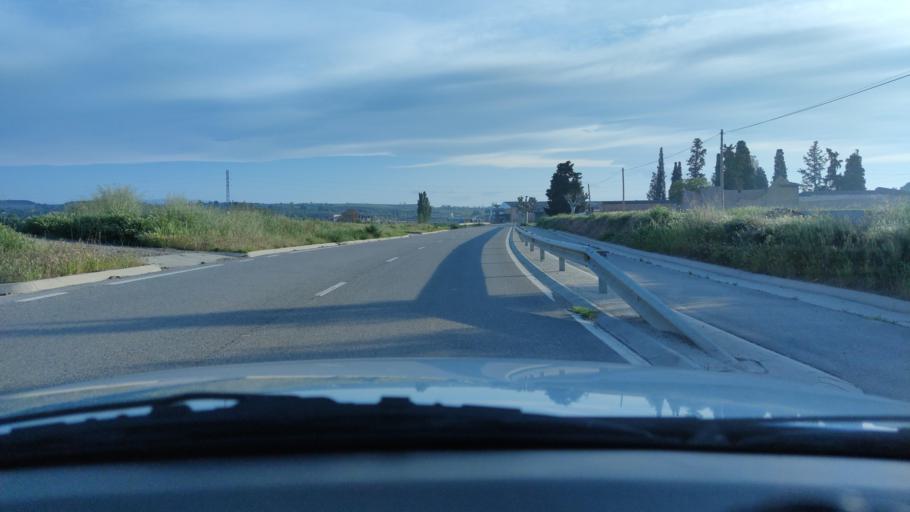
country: ES
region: Catalonia
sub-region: Provincia de Lleida
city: Castellsera
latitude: 41.7502
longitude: 0.9914
